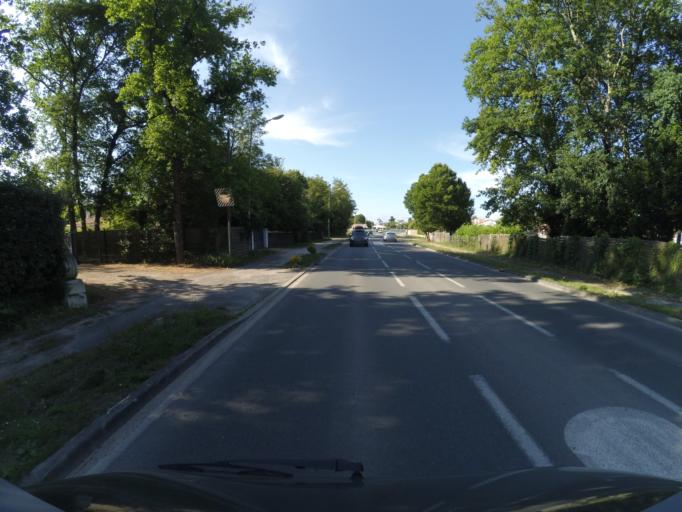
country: FR
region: Poitou-Charentes
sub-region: Departement de la Charente-Maritime
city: Saint-Sulpice-de-Royan
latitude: 45.6555
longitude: -1.0230
